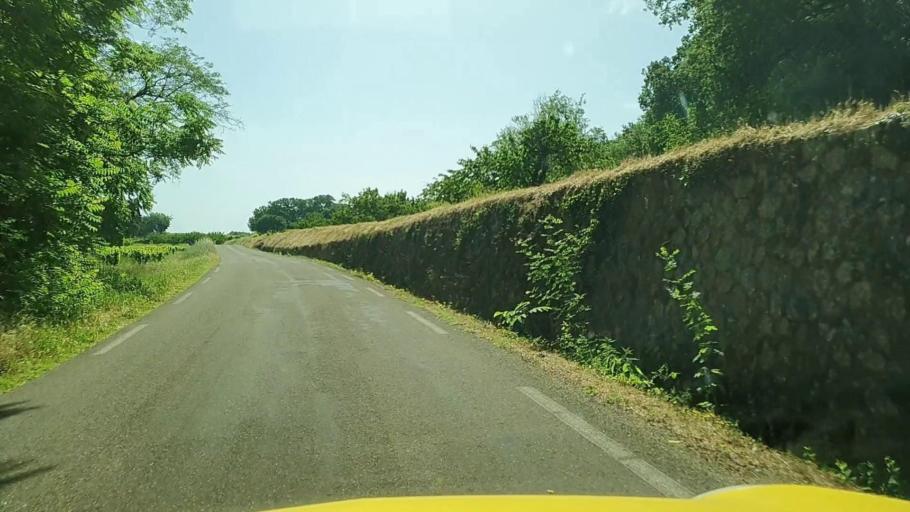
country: FR
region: Languedoc-Roussillon
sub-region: Departement du Gard
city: Tresques
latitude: 44.0937
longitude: 4.5578
